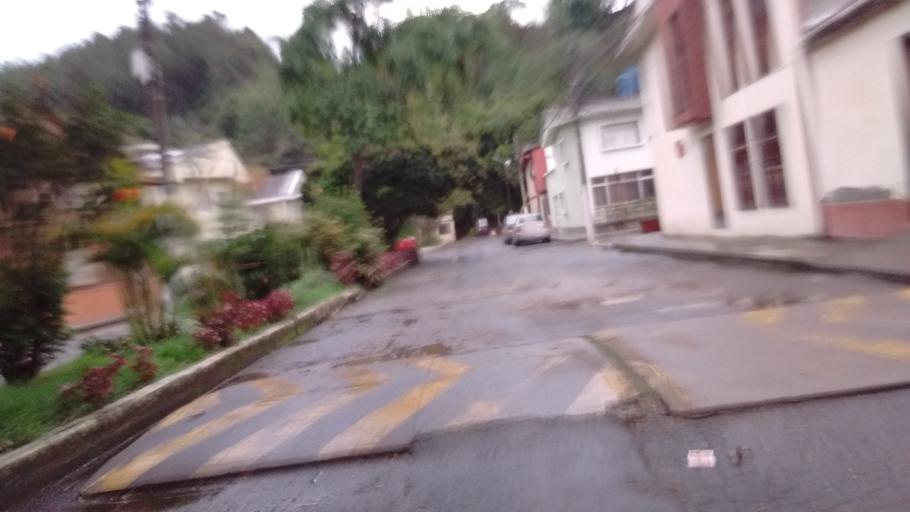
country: CO
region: Cauca
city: Popayan
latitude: 2.4434
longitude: -76.6004
